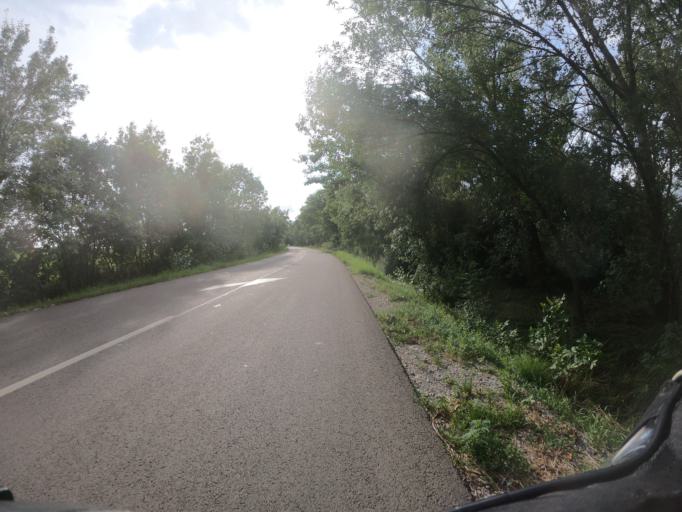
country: HU
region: Borsod-Abauj-Zemplen
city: Mezocsat
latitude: 47.8271
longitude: 20.8472
